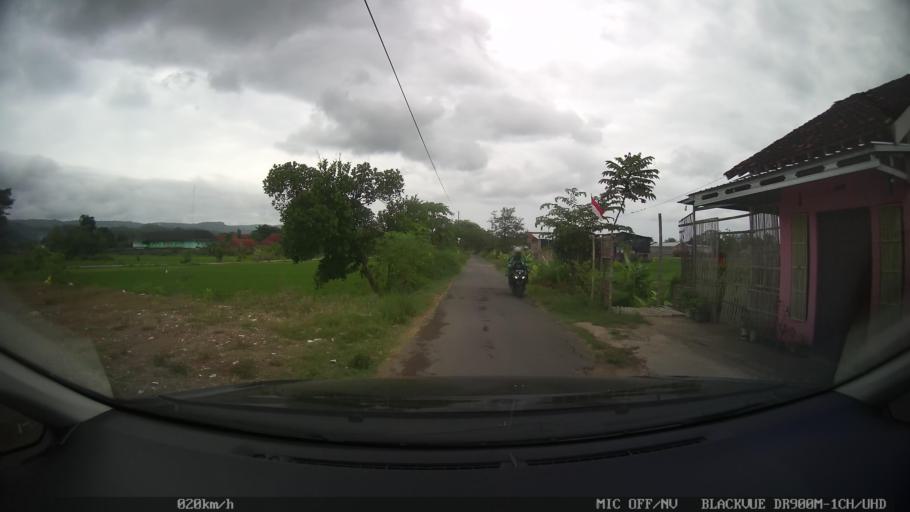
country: ID
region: Daerah Istimewa Yogyakarta
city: Sewon
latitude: -7.8548
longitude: 110.4160
